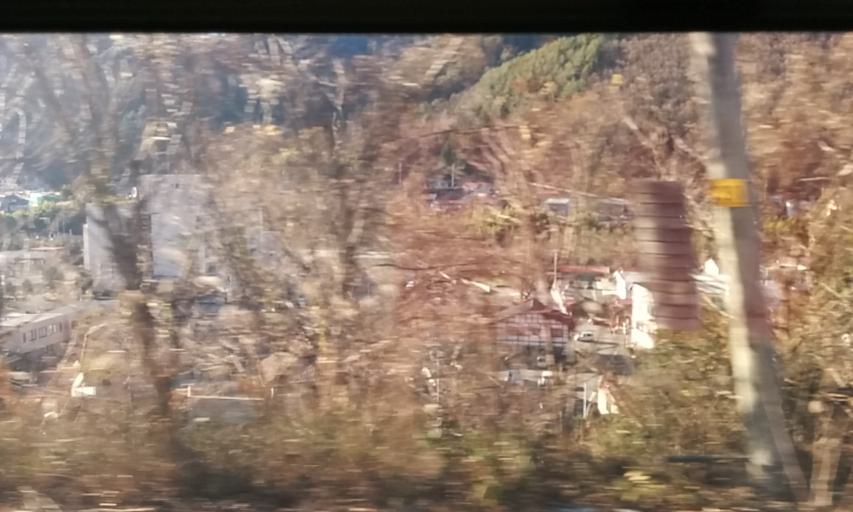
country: JP
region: Nagano
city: Ina
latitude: 35.8392
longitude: 137.6904
